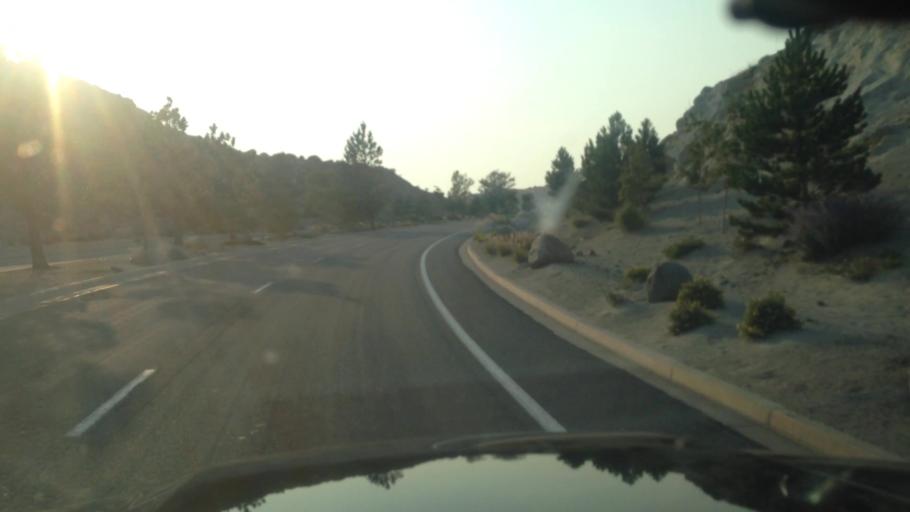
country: US
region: Nevada
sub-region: Washoe County
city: Mogul
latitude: 39.5192
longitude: -119.9067
